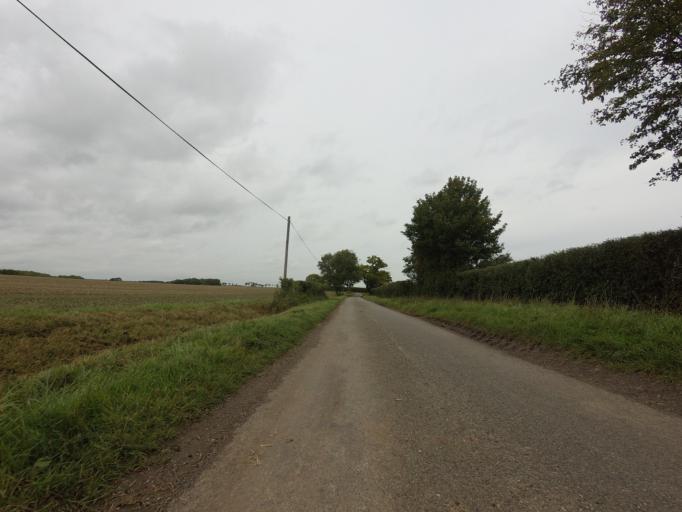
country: GB
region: England
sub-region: Hertfordshire
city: Reed
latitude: 51.9789
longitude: 0.0914
